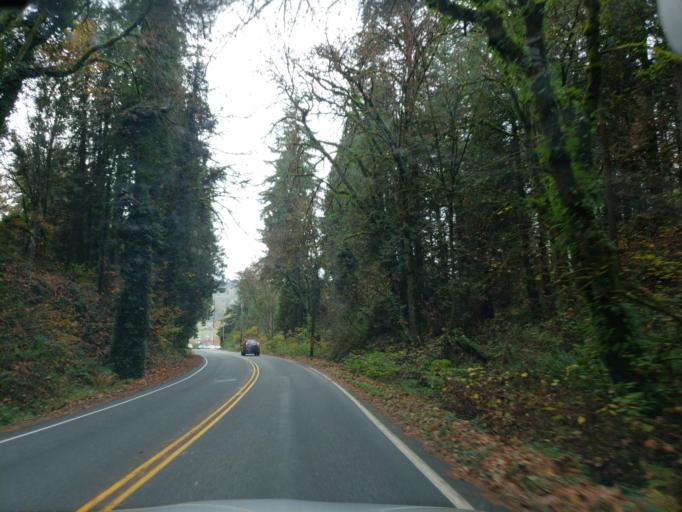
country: US
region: Washington
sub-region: King County
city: Woodinville
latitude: 47.7332
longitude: -122.1381
